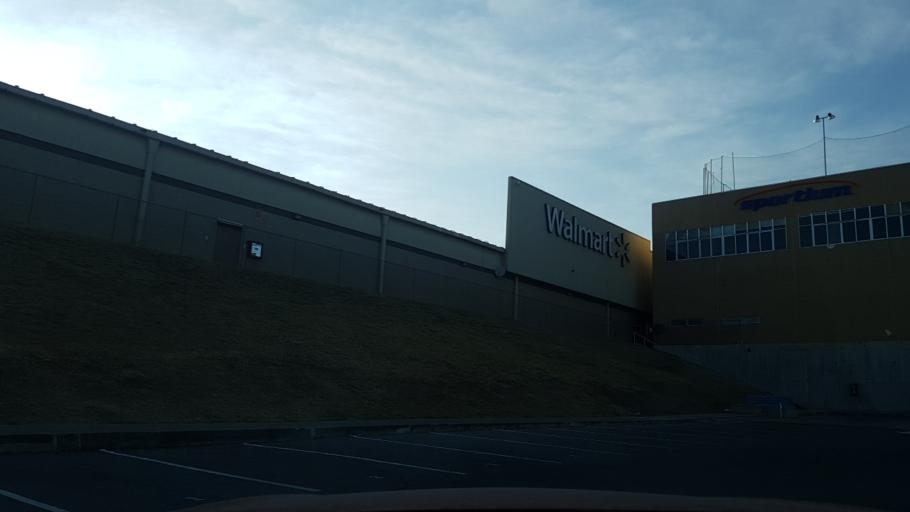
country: MX
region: Mexico
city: Cuautitlan Izcalli
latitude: 19.6387
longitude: -99.2224
